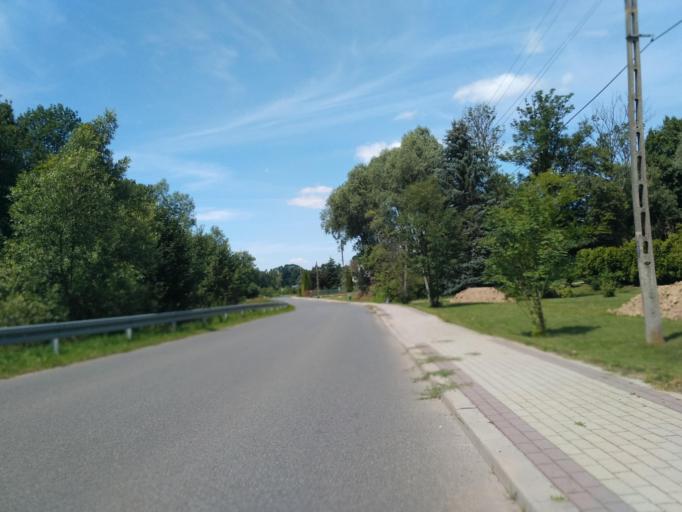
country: PL
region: Subcarpathian Voivodeship
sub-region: Powiat krosnienski
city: Kroscienko Wyzne
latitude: 49.6831
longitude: 21.8065
